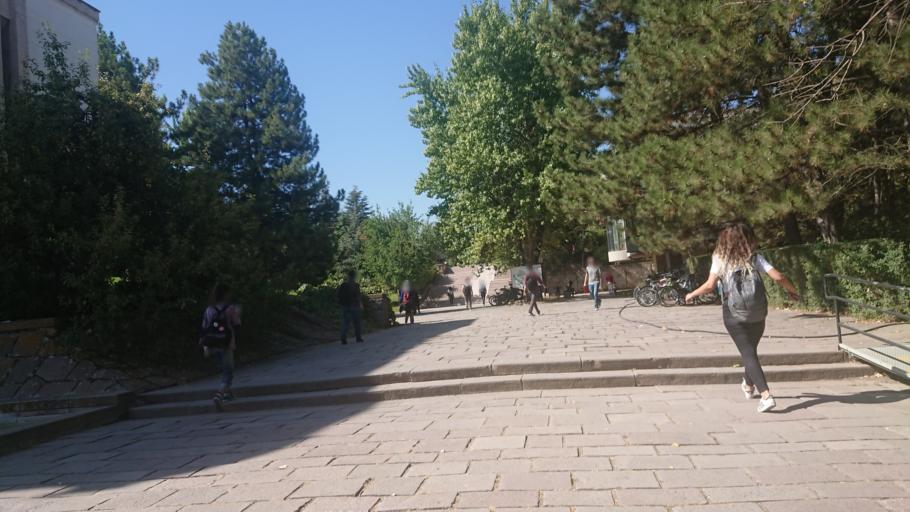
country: TR
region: Ankara
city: Ankara
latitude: 39.8952
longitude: 32.7840
